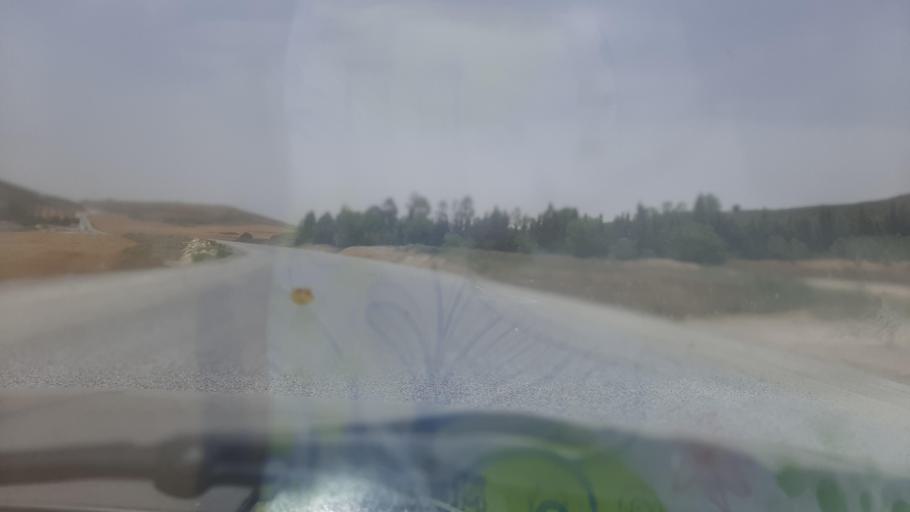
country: TN
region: Tunis
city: La Mohammedia
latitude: 36.5440
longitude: 10.1513
